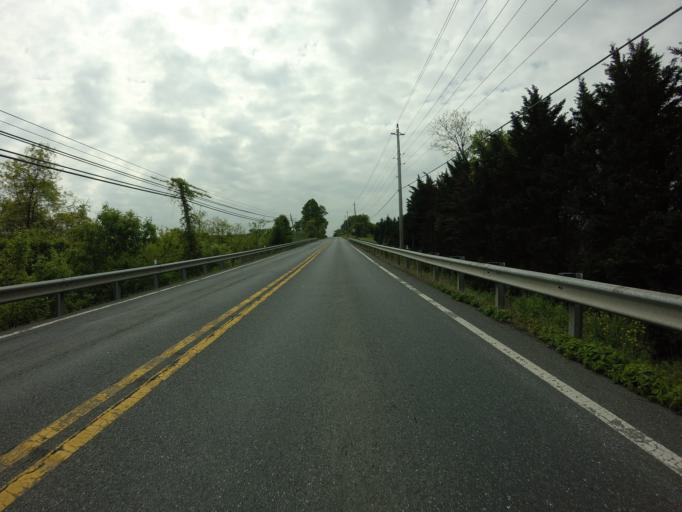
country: US
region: Maryland
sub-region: Frederick County
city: Urbana
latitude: 39.3156
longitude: -77.3315
